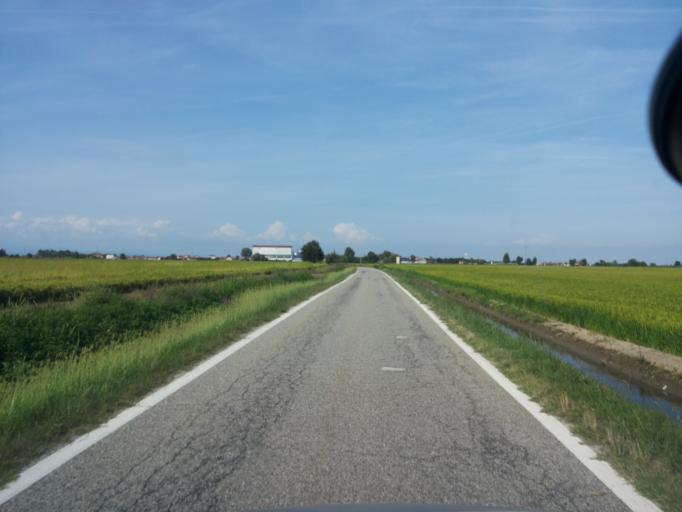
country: IT
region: Piedmont
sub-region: Provincia di Vercelli
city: San Germano Vercellese
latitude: 45.3396
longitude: 8.2376
